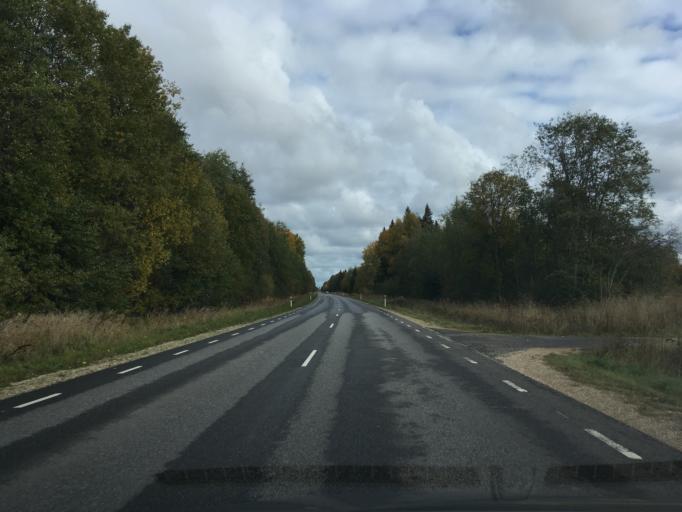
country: EE
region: Harju
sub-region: Anija vald
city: Kehra
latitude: 59.2267
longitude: 25.2745
